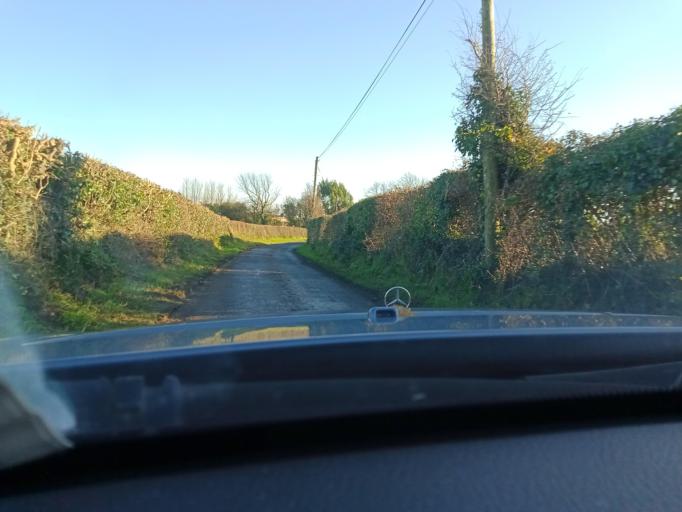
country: IE
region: Leinster
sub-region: Kilkenny
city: Mooncoin
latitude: 52.2949
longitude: -7.1849
